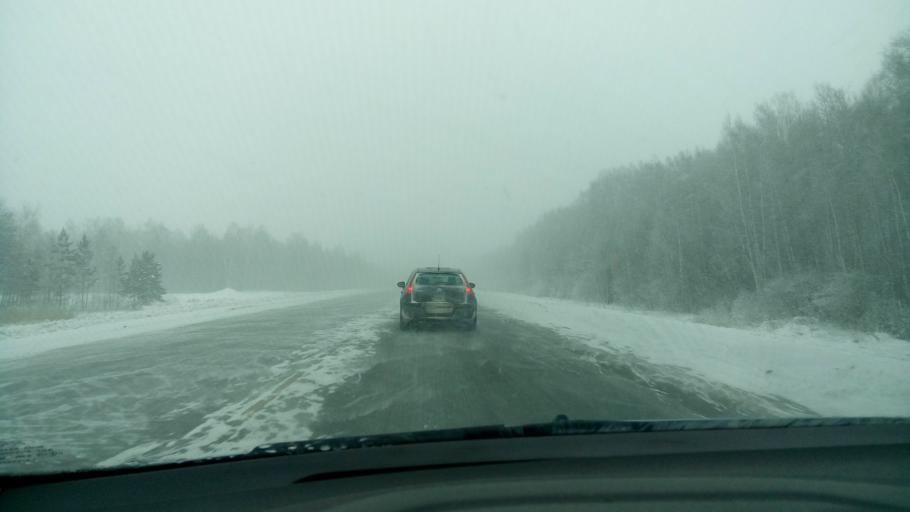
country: RU
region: Sverdlovsk
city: Bogdanovich
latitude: 56.7747
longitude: 61.9627
